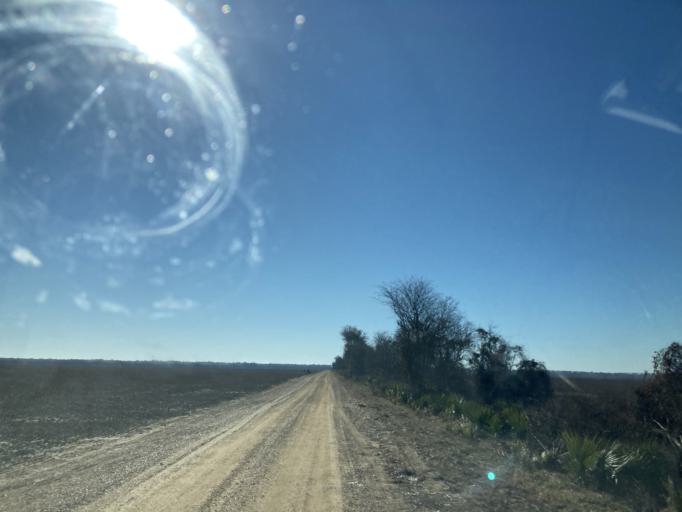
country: US
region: Mississippi
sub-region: Sharkey County
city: Rolling Fork
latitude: 32.8490
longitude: -90.6723
